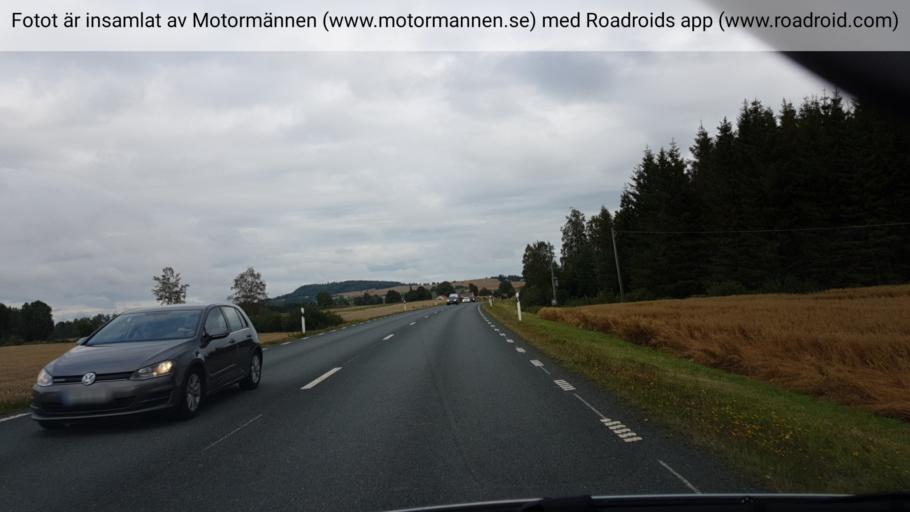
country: SE
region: Vaestra Goetaland
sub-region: Falkopings Kommun
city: Akarp
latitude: 58.1255
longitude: 13.7208
